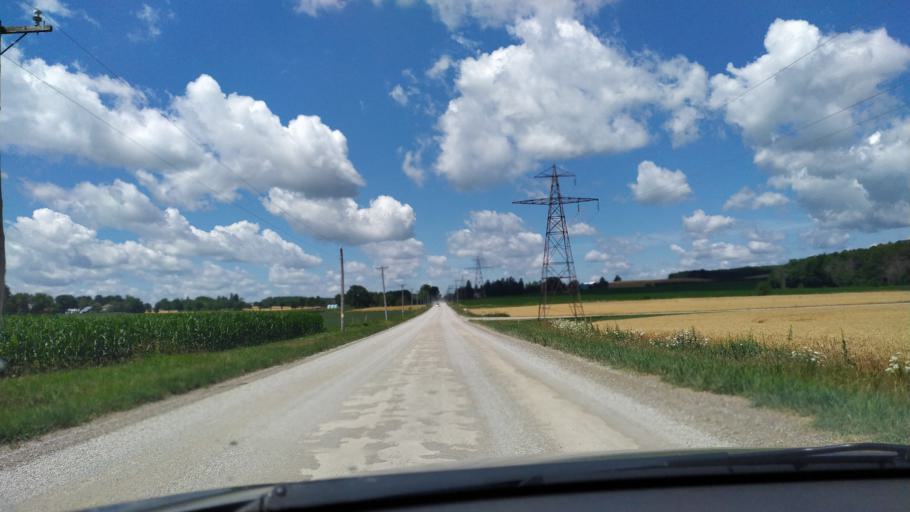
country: CA
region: Ontario
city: Stratford
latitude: 43.3874
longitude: -80.7708
